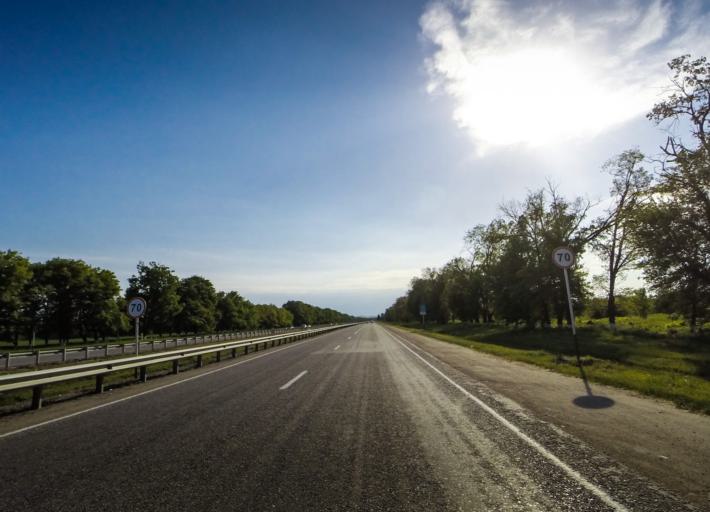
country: RU
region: Kabardino-Balkariya
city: Nartan
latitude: 43.4919
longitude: 43.6897
